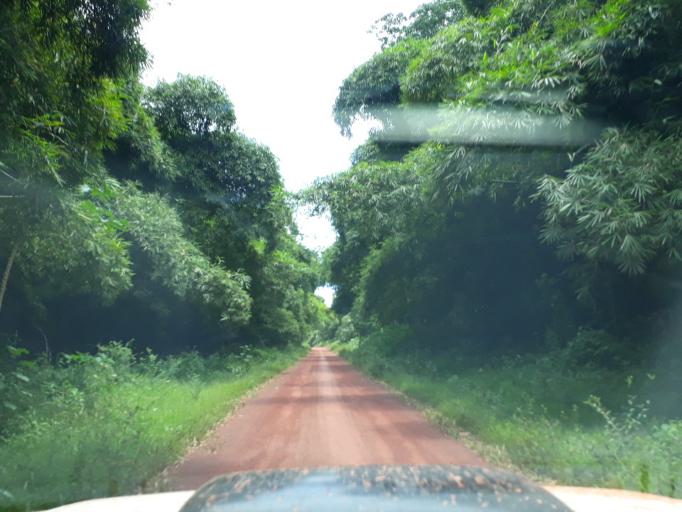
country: CD
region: Eastern Province
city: Buta
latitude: 2.5644
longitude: 24.8256
